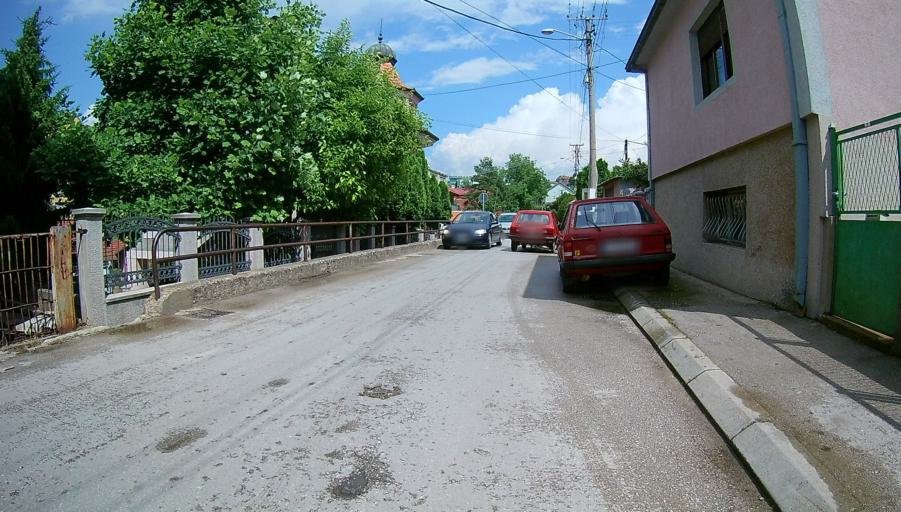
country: RS
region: Central Serbia
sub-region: Nisavski Okrug
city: Nis
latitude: 43.3092
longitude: 21.8941
